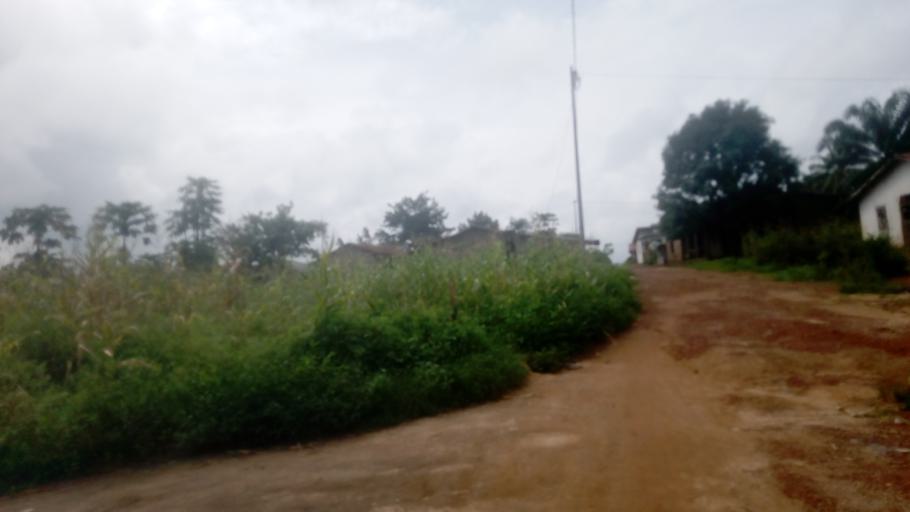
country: SL
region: Northern Province
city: Lunsar
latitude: 8.6931
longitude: -12.5378
